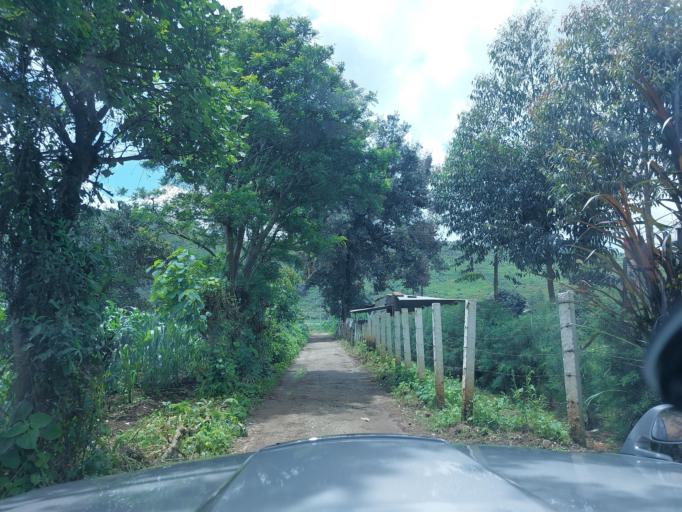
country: GT
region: Chimaltenango
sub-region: Municipio de Chimaltenango
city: Chimaltenango
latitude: 14.6447
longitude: -90.8255
